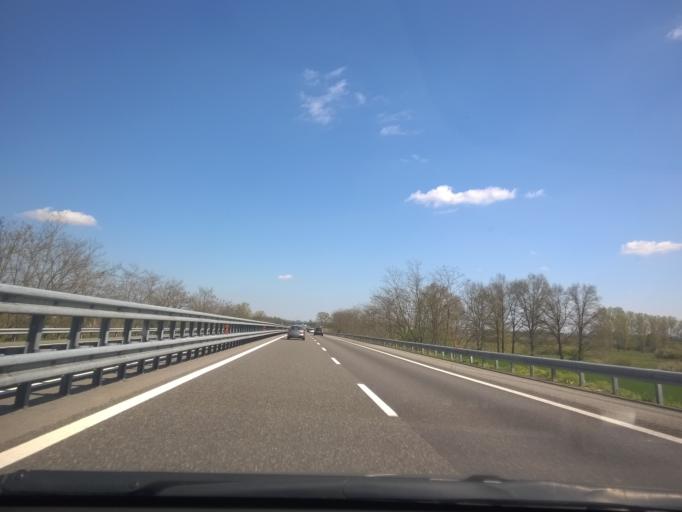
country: IT
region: Emilia-Romagna
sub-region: Provincia di Piacenza
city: Sarmato
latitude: 45.0691
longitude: 9.5048
